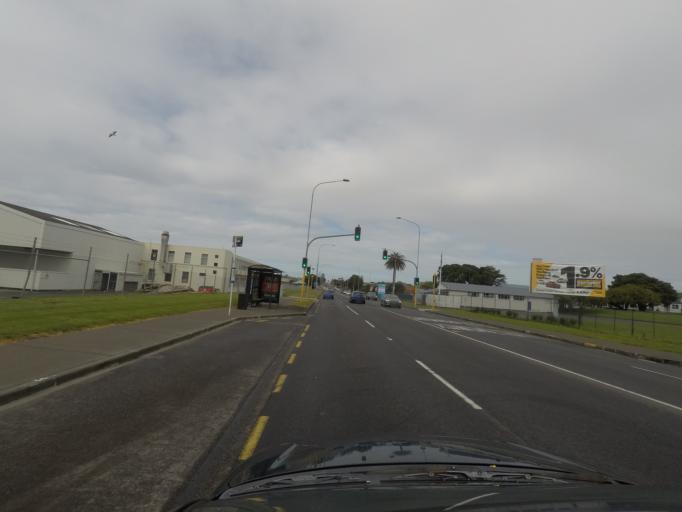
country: NZ
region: Auckland
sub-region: Auckland
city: Tamaki
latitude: -36.9009
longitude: 174.8435
